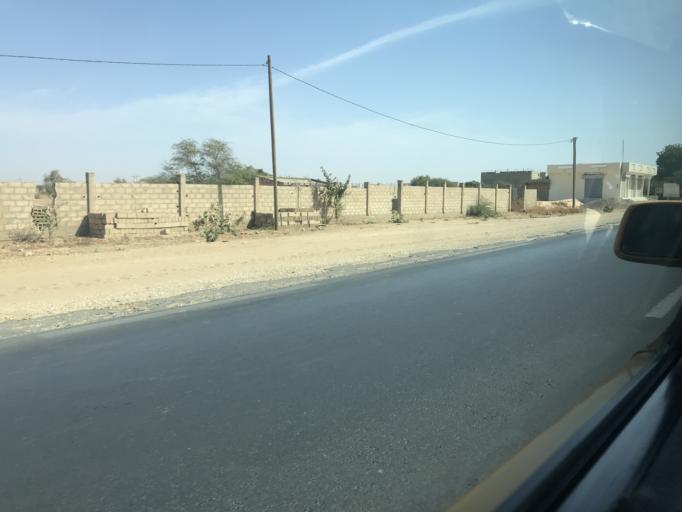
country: SN
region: Saint-Louis
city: Saint-Louis
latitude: 16.0536
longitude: -16.4283
